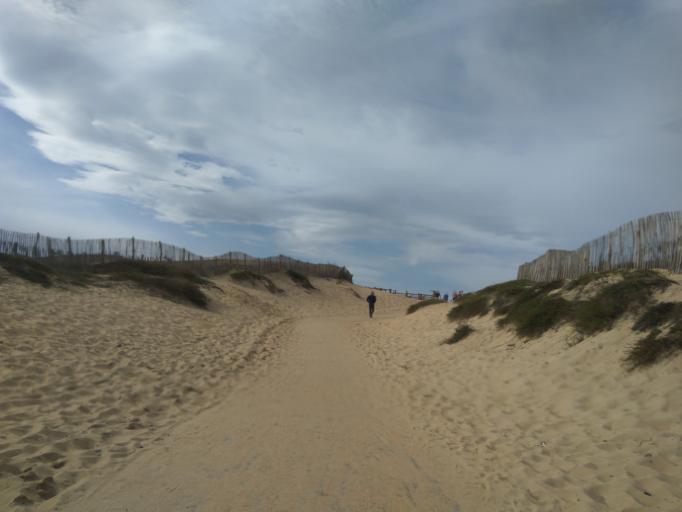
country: FR
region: Aquitaine
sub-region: Departement des Landes
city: Capbreton
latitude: 43.6364
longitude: -1.4477
